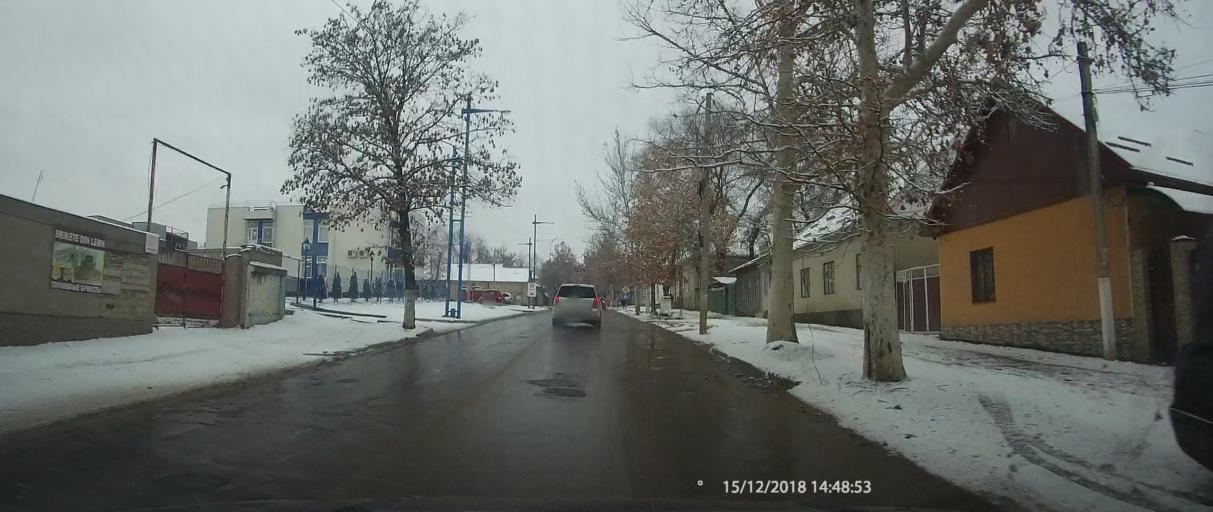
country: MD
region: Cahul
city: Cahul
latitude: 45.9006
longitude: 28.1959
